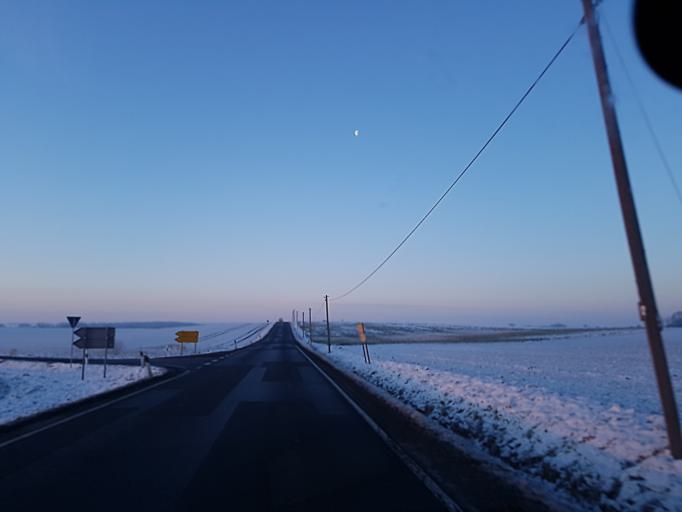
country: DE
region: Saxony
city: Oschatz
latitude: 51.2791
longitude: 13.1278
